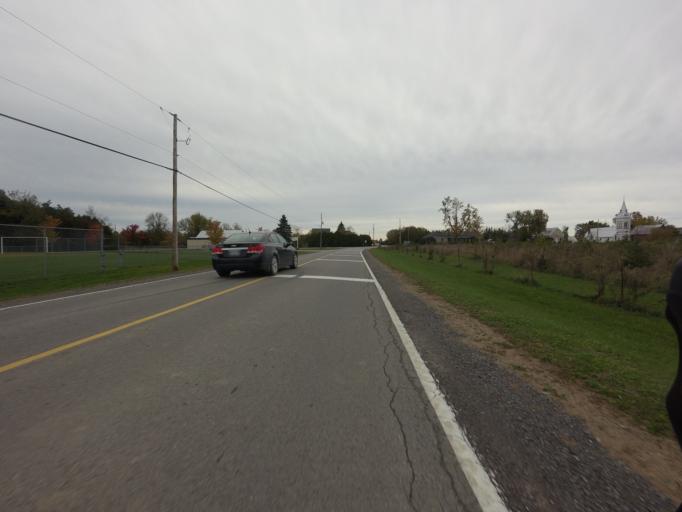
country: CA
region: Ontario
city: Bells Corners
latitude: 45.0909
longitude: -75.7559
